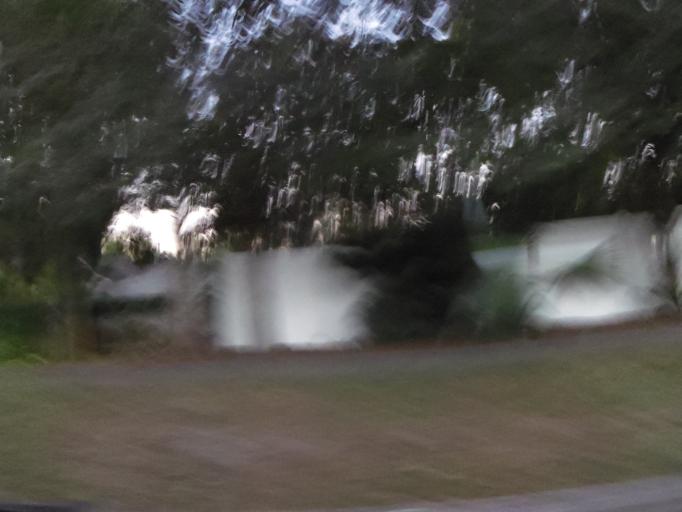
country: US
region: Florida
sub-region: Duval County
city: Jacksonville
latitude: 30.3121
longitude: -81.7222
